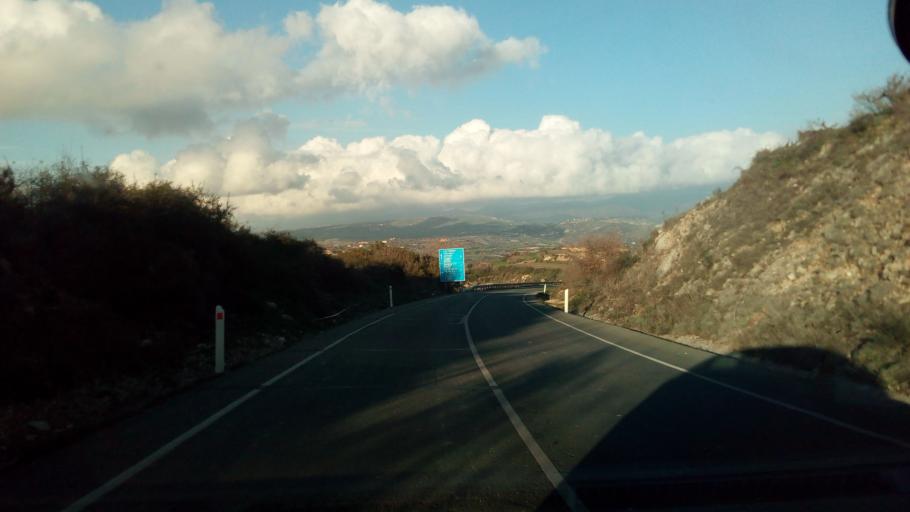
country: CY
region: Pafos
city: Mesogi
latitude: 34.8579
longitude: 32.4968
